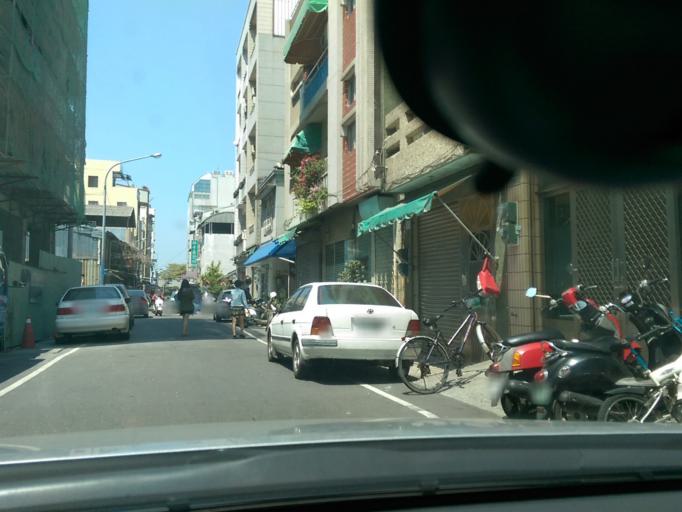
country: TW
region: Taiwan
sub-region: Chiayi
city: Jiayi Shi
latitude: 23.4828
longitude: 120.4501
